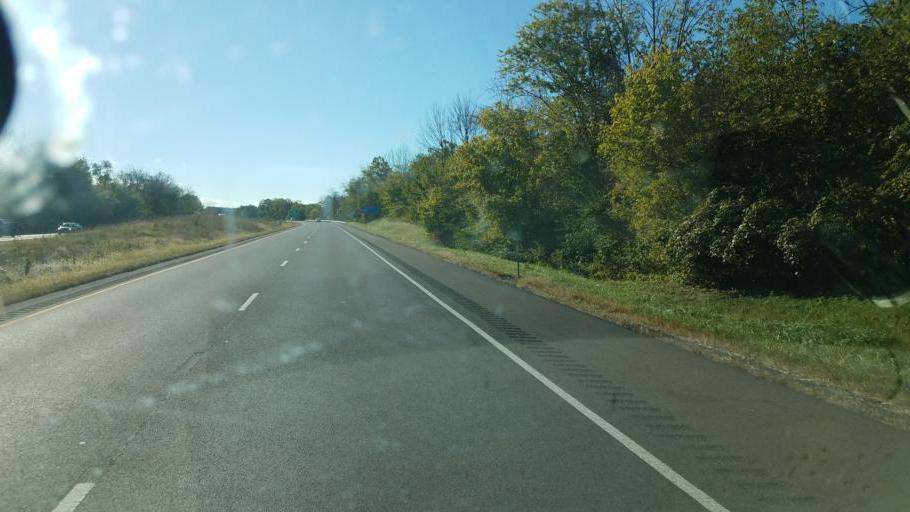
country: US
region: Maryland
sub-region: Washington County
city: Hancock
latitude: 39.6345
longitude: -78.0243
